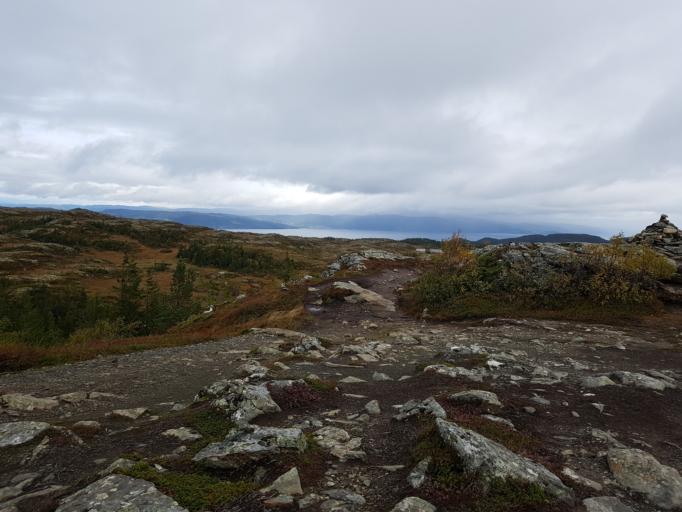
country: NO
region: Sor-Trondelag
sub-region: Melhus
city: Melhus
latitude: 63.4029
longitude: 10.2016
